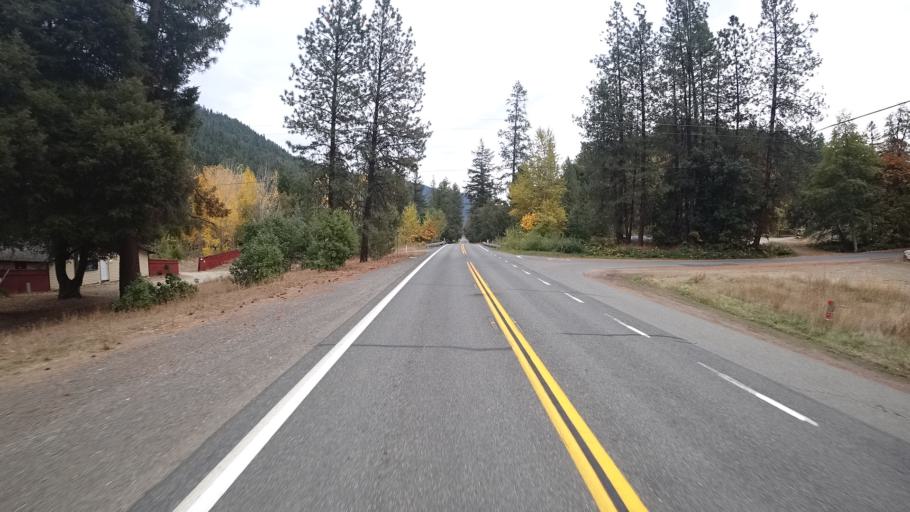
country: US
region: California
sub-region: Siskiyou County
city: Happy Camp
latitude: 41.8354
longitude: -123.1726
